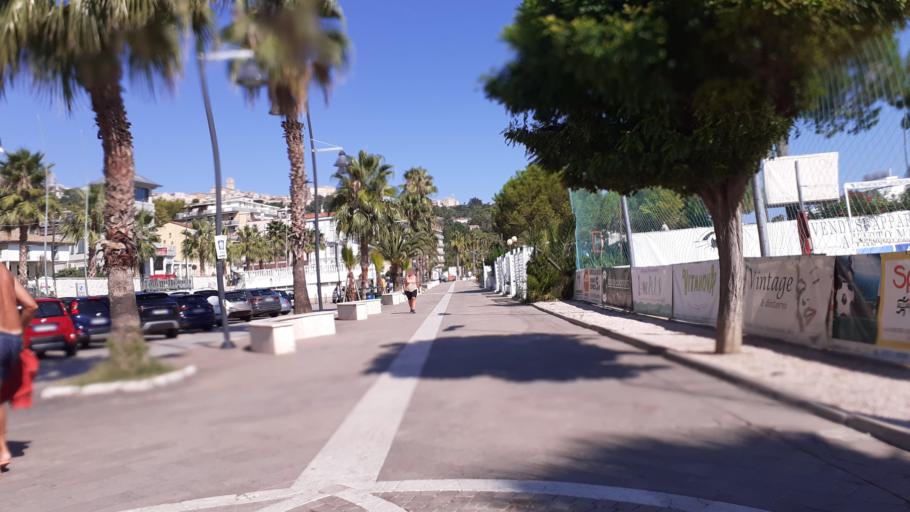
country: IT
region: Abruzzo
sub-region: Provincia di Chieti
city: Marina di Vasto
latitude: 42.1025
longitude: 14.7188
